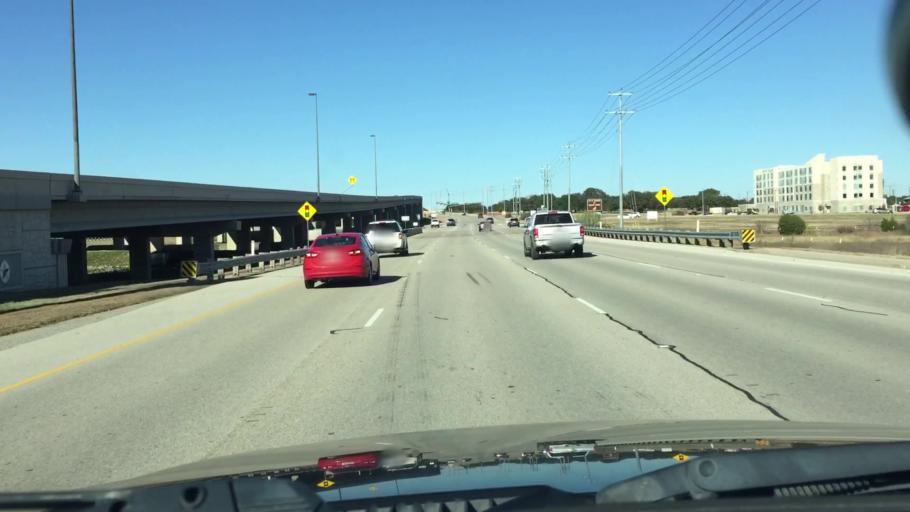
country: US
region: Texas
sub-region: Williamson County
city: Cedar Park
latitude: 30.5343
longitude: -97.8164
